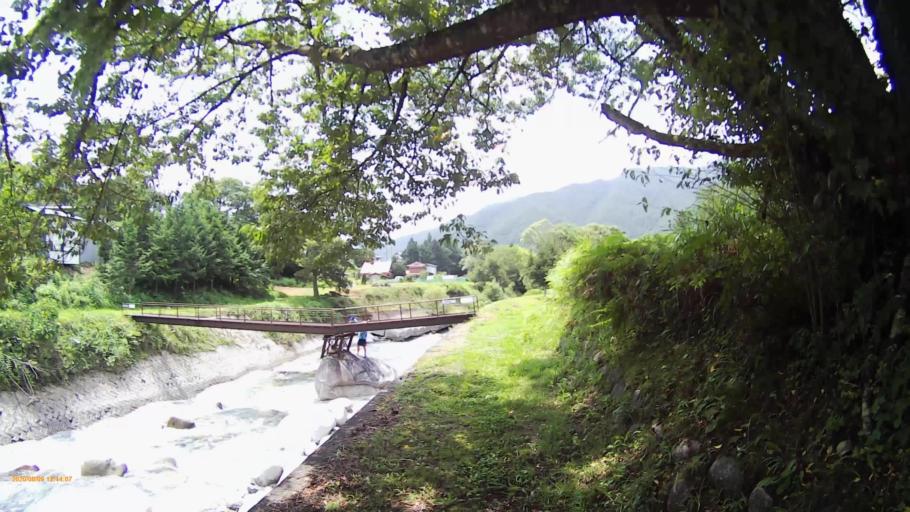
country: JP
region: Nagano
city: Ina
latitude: 35.8649
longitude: 137.7320
